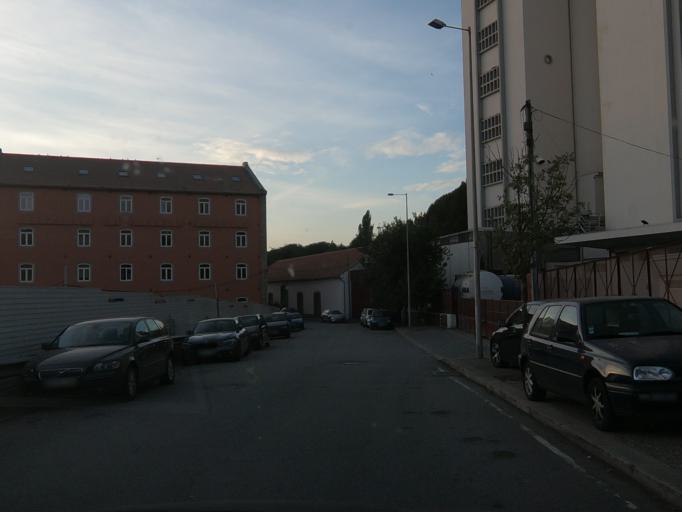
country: PT
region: Porto
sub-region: Gondomar
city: Valbom
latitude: 41.1420
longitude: -8.5734
